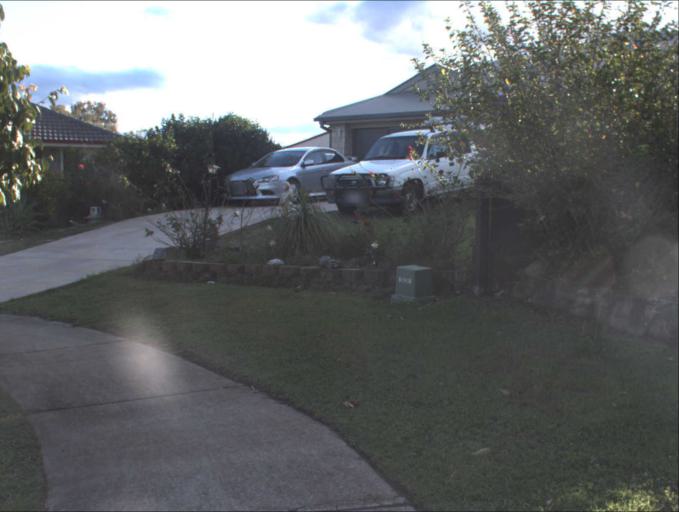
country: AU
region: Queensland
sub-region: Logan
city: North Maclean
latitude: -27.8042
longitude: 152.9571
